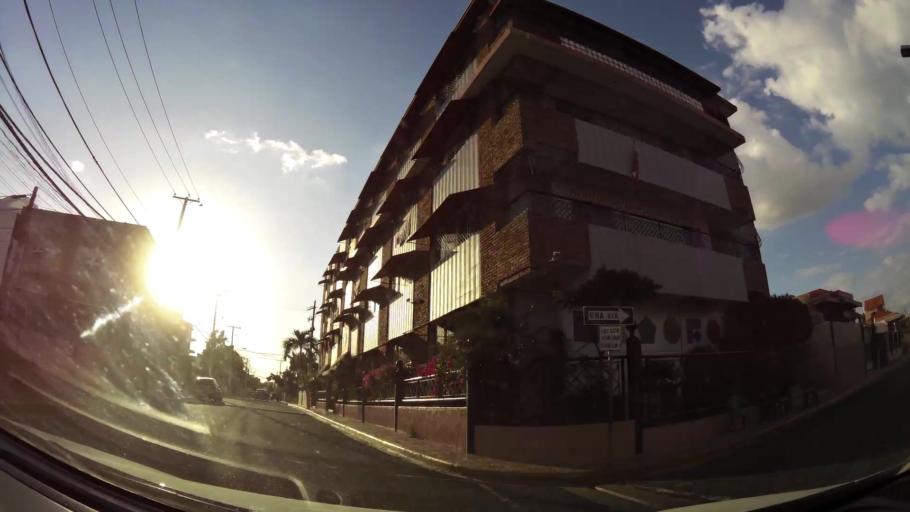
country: DO
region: Santo Domingo
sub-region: Santo Domingo
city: Santo Domingo Este
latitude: 18.4794
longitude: -69.8326
